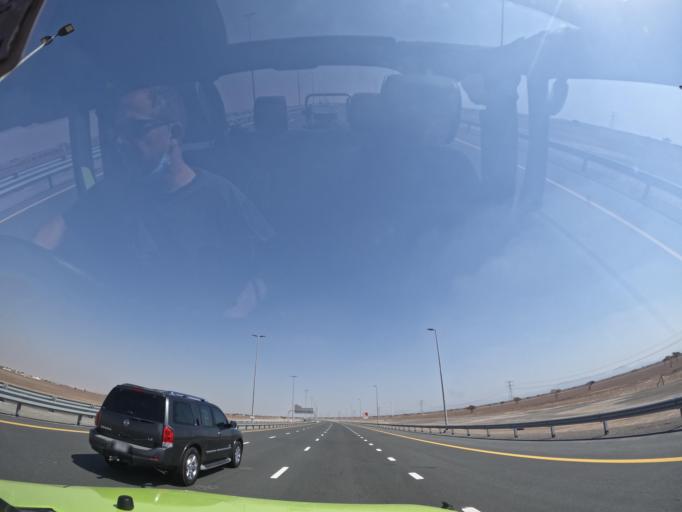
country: AE
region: Ash Shariqah
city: Adh Dhayd
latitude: 24.9370
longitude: 55.8234
